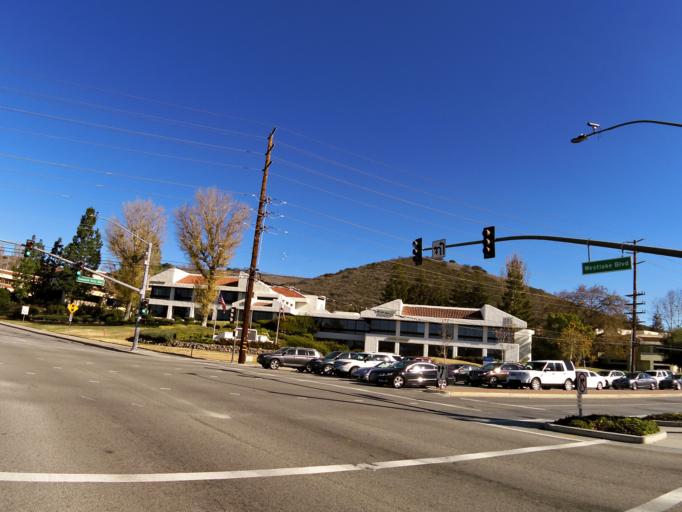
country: US
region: California
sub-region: Ventura County
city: Thousand Oaks
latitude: 34.1607
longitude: -118.8229
